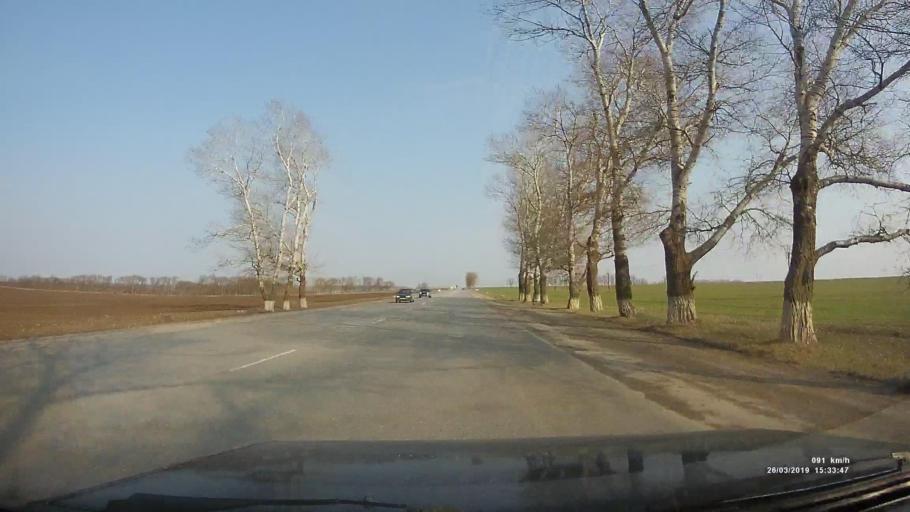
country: RU
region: Rostov
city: Sinyavskoye
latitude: 47.3013
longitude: 39.1804
